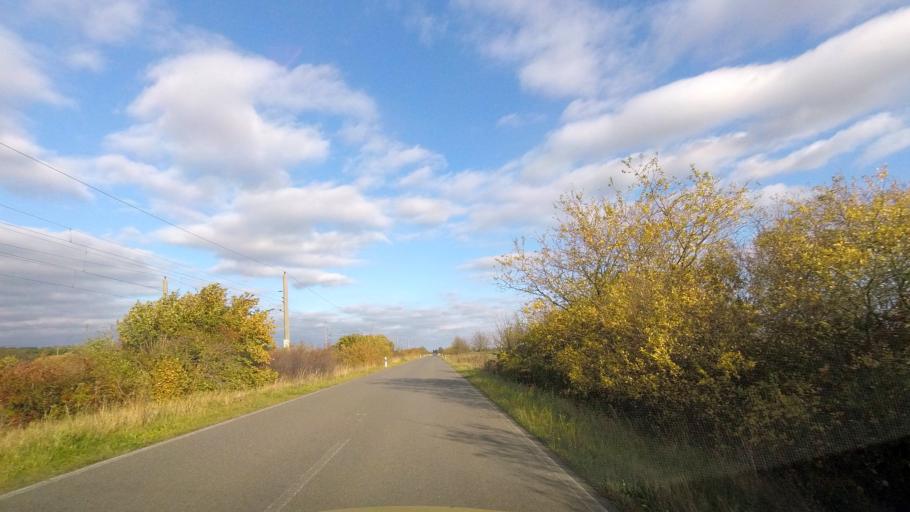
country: DE
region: Saxony-Anhalt
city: Seyda
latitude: 51.9510
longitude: 12.8714
